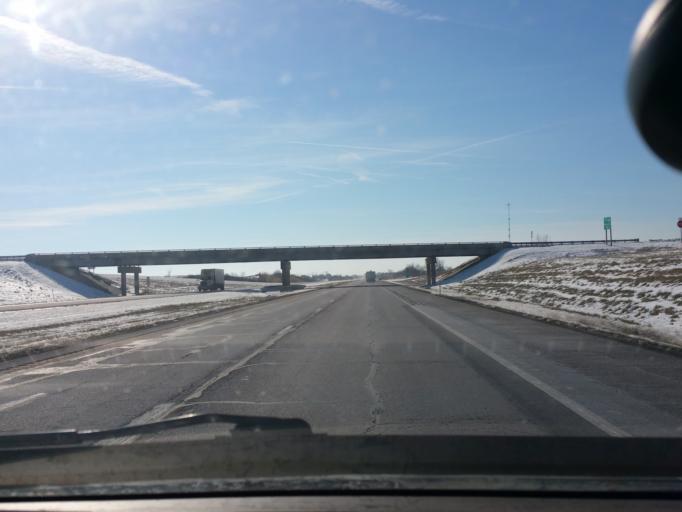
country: US
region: Missouri
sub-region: Harrison County
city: Bethany
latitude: 40.3755
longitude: -94.0029
